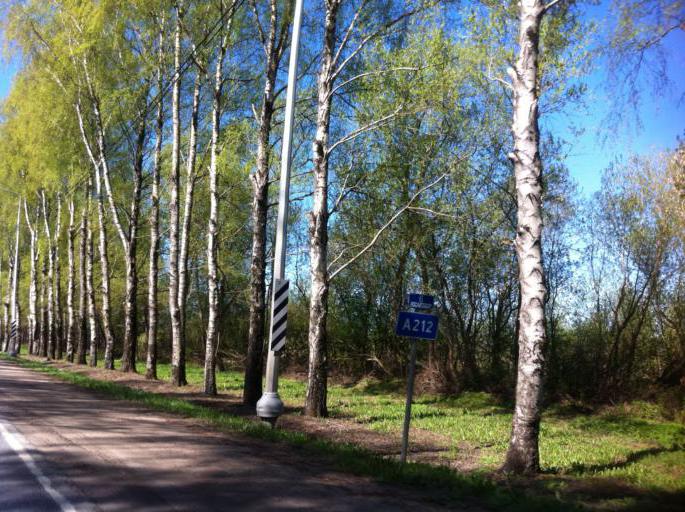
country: RU
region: Pskov
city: Pskov
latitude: 57.7998
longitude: 28.2390
